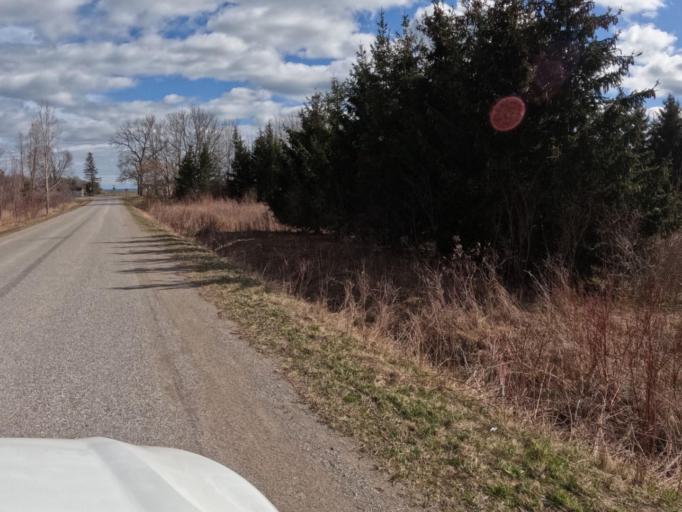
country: CA
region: Ontario
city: Norfolk County
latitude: 42.7510
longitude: -80.2745
